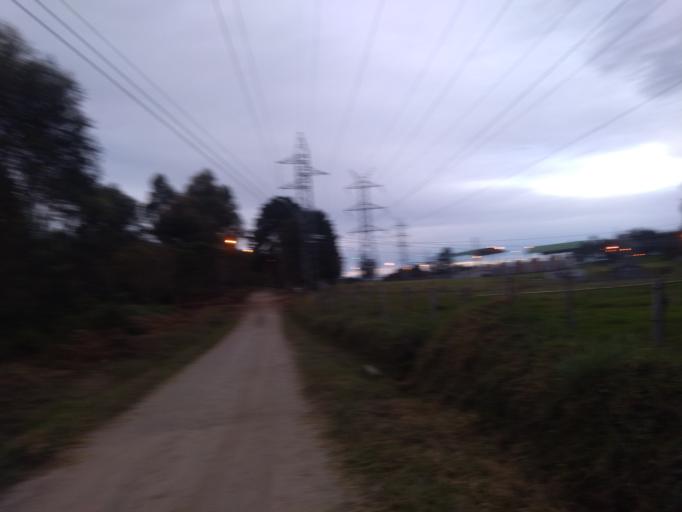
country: CO
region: Antioquia
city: Bello
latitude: 6.3549
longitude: -75.6074
